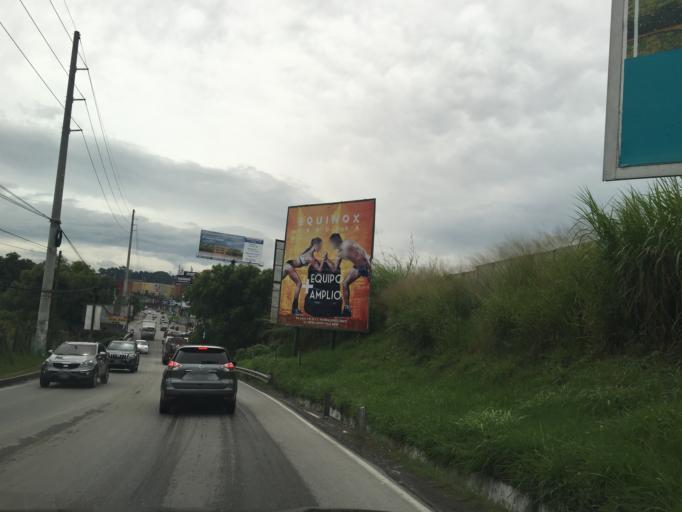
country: GT
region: Guatemala
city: Petapa
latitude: 14.5251
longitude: -90.5606
